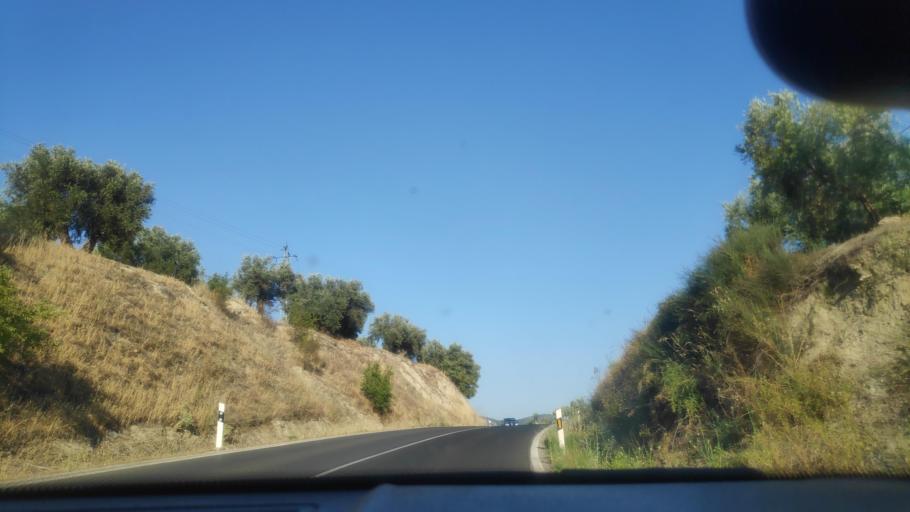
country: ES
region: Andalusia
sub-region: Provincia de Jaen
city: Jaen
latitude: 37.7480
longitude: -3.7873
